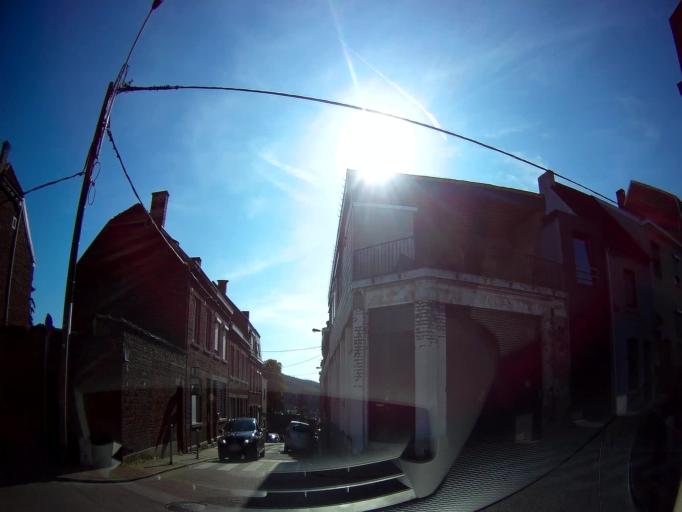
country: BE
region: Wallonia
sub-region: Province de Liege
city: Huy
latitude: 50.5269
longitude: 5.2290
